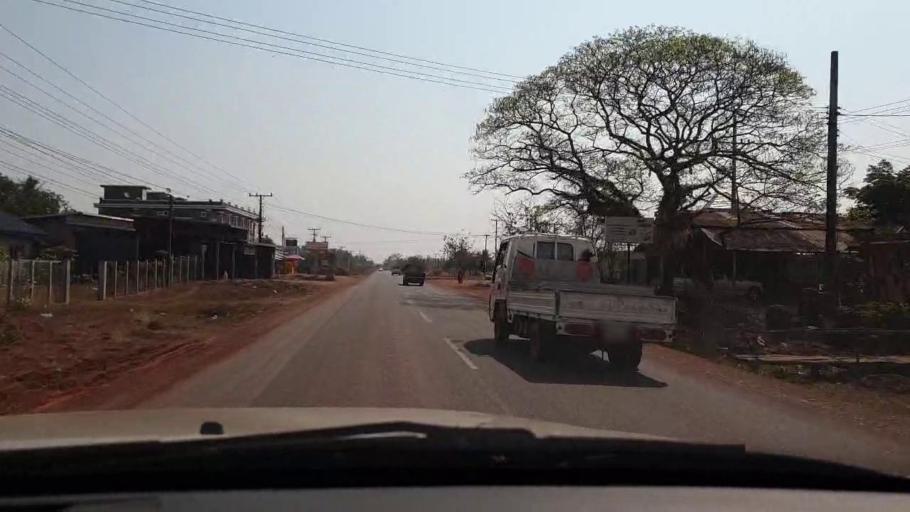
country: TH
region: Nong Khai
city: Nong Khai
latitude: 18.0542
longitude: 102.8376
